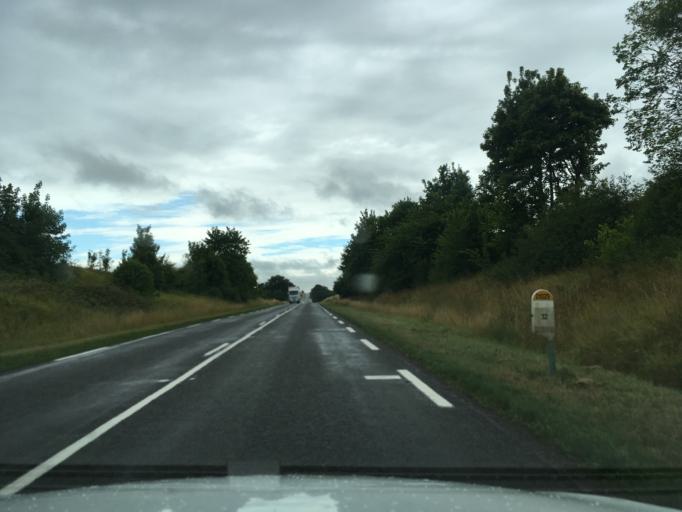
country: FR
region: Picardie
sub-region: Departement de l'Aisne
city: Origny-Sainte-Benoite
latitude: 49.8530
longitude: 3.5250
